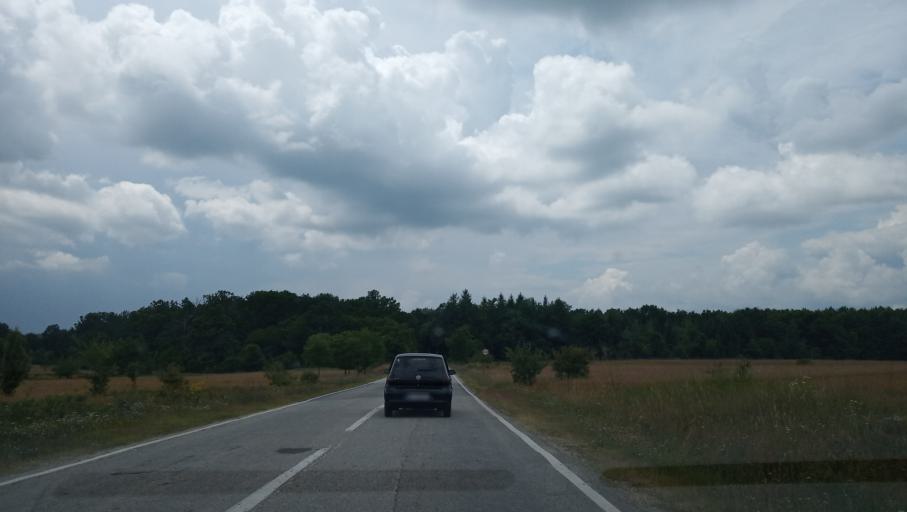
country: RO
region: Gorj
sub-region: Comuna Pestisani
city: Pestisani
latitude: 45.0579
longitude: 23.0103
